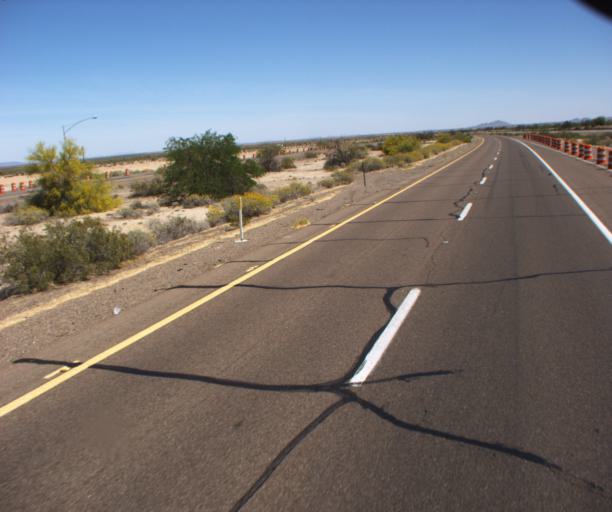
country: US
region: Arizona
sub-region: Yuma County
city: Wellton
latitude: 32.7314
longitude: -113.7125
